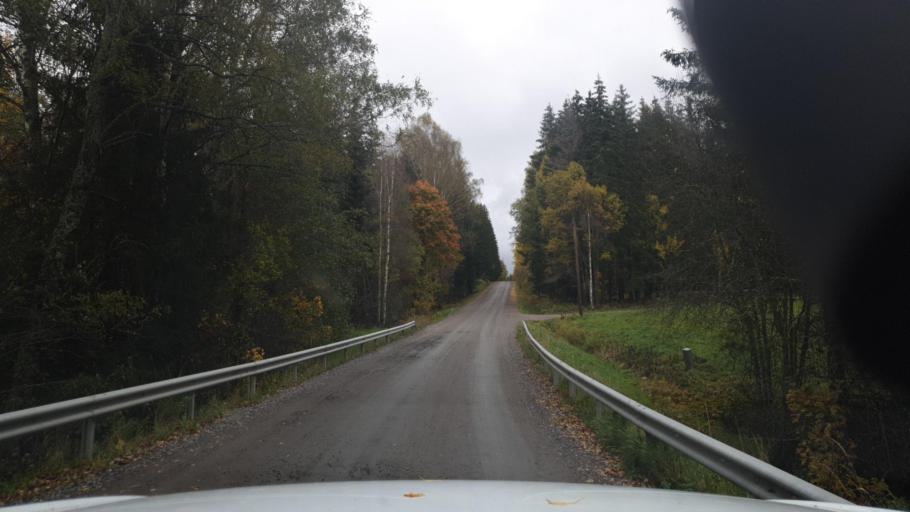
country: SE
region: Vaermland
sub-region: Karlstads Kommun
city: Edsvalla
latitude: 59.5031
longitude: 13.1943
